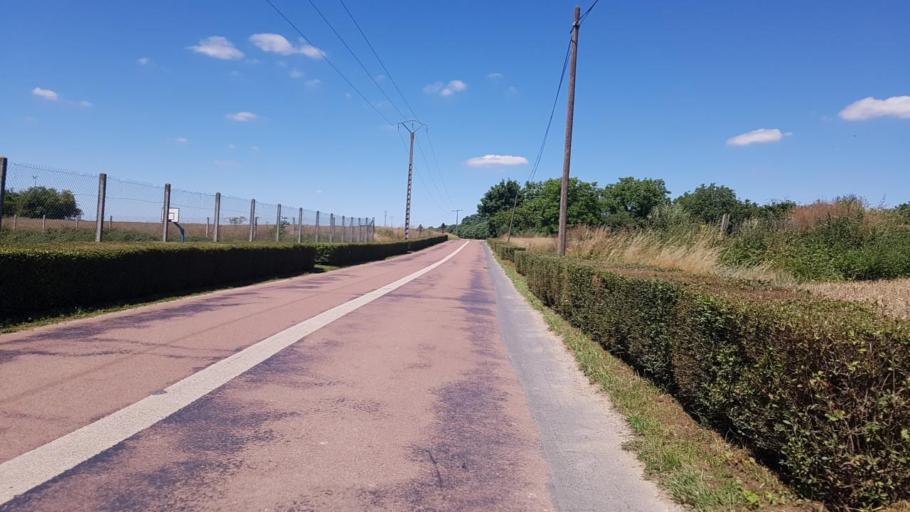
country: FR
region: Ile-de-France
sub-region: Departement de Seine-et-Marne
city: Sammeron
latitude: 48.9566
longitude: 3.0648
